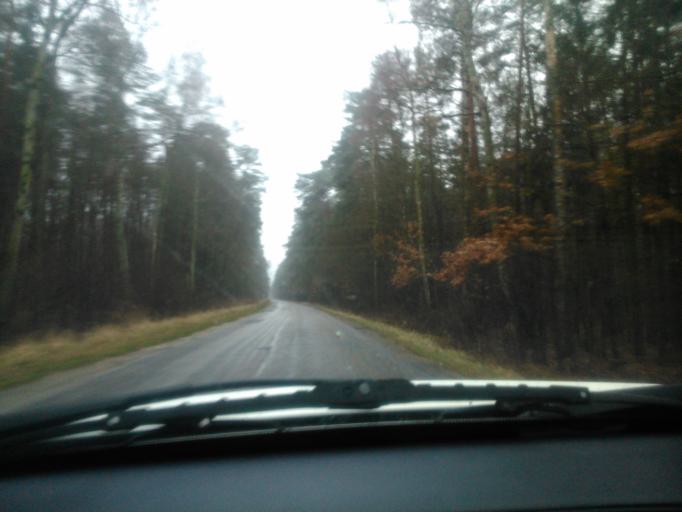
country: PL
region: Kujawsko-Pomorskie
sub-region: Powiat wabrzeski
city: Debowa Laka
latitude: 53.1903
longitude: 19.1532
